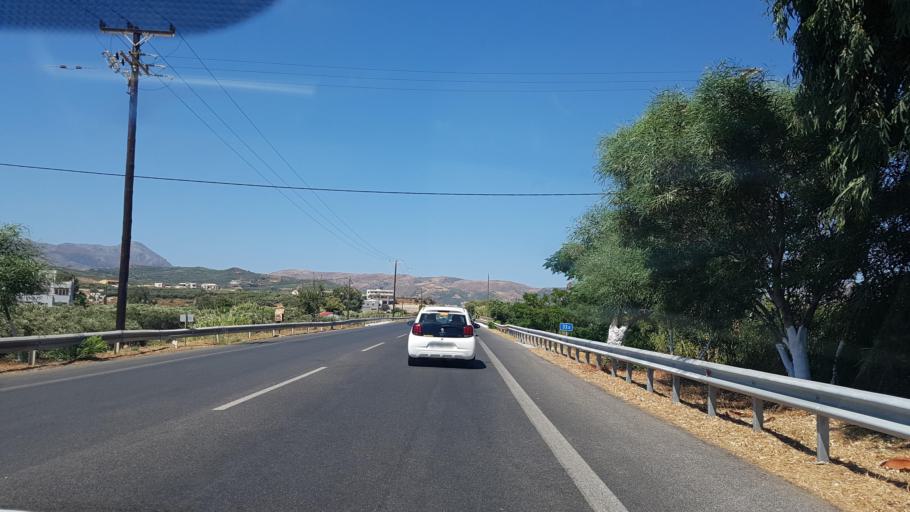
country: GR
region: Crete
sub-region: Nomos Chanias
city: Kissamos
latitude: 35.4968
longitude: 23.6917
